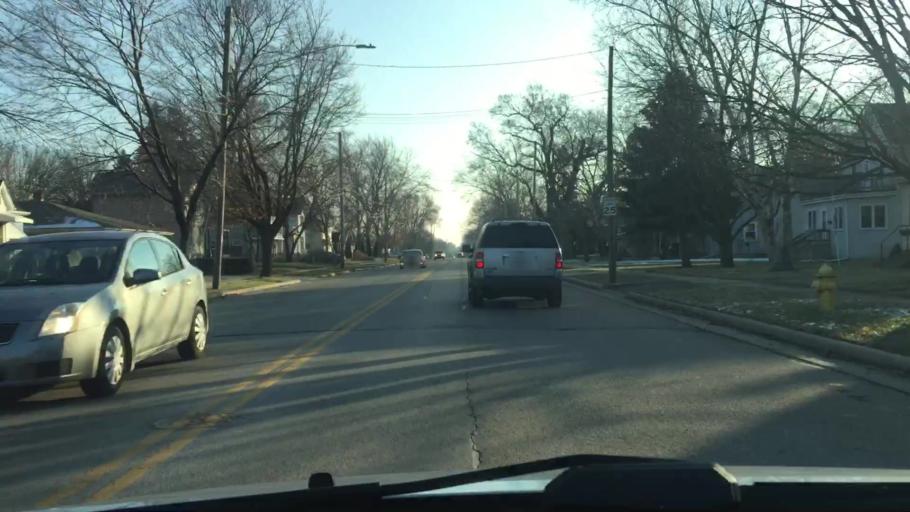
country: US
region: Wisconsin
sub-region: Waukesha County
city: Oconomowoc
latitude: 43.1014
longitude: -88.4958
